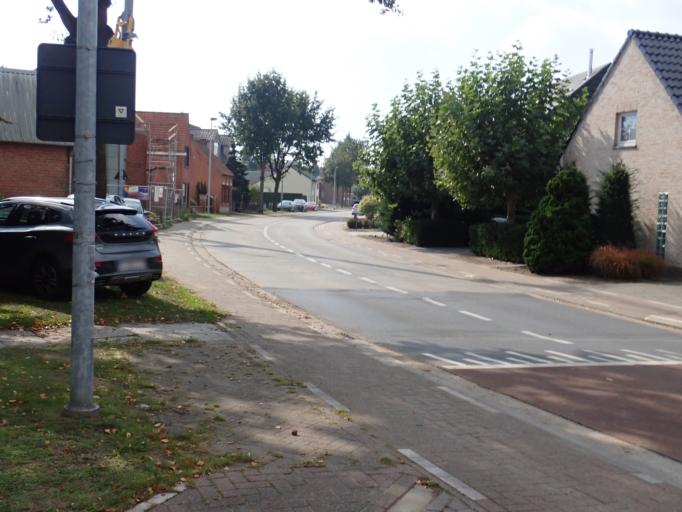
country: BE
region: Flanders
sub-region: Provincie Oost-Vlaanderen
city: Stekene
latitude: 51.2334
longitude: 4.0446
